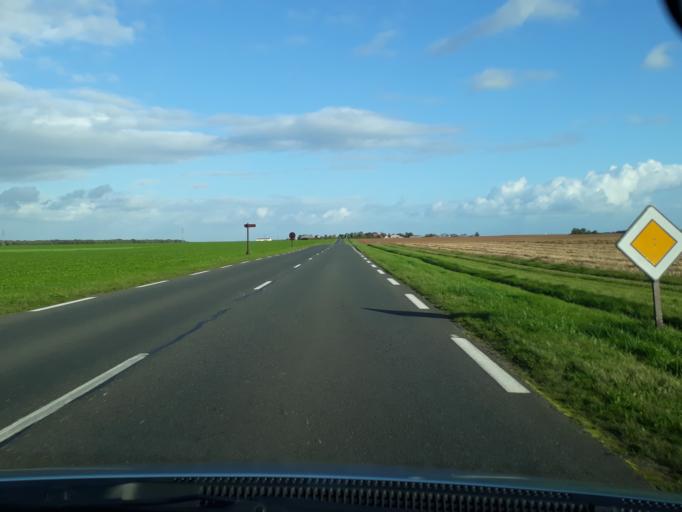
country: FR
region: Centre
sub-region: Departement du Loiret
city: Malesherbes
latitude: 48.3070
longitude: 2.4529
